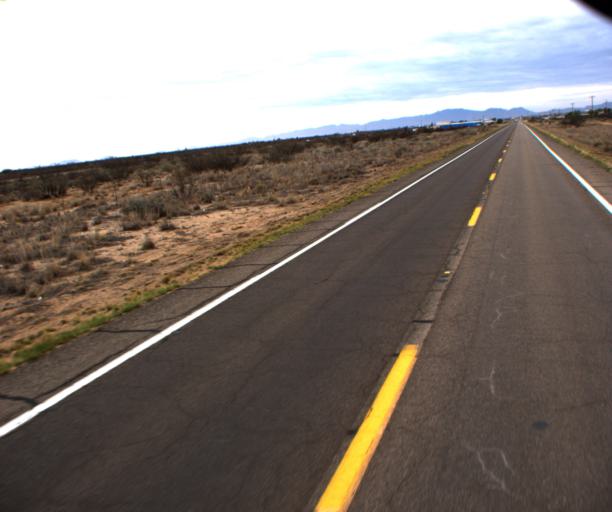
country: US
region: Arizona
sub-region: Cochise County
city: Willcox
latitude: 32.2852
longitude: -109.8099
